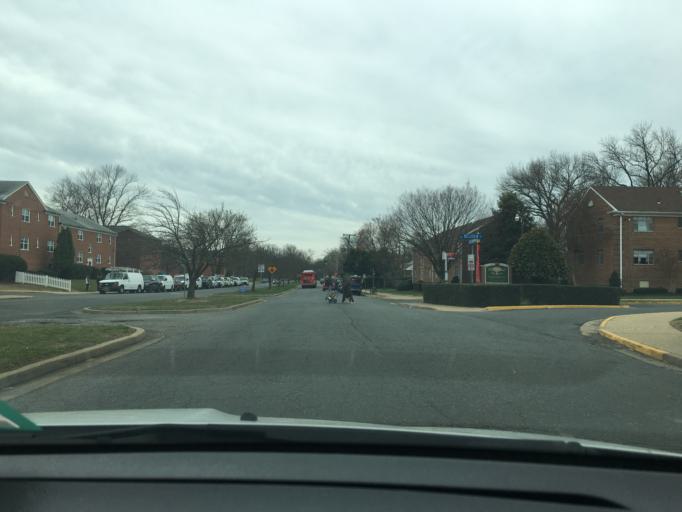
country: US
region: Virginia
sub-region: Fairfax County
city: Baileys Crossroads
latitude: 38.8542
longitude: -77.1401
